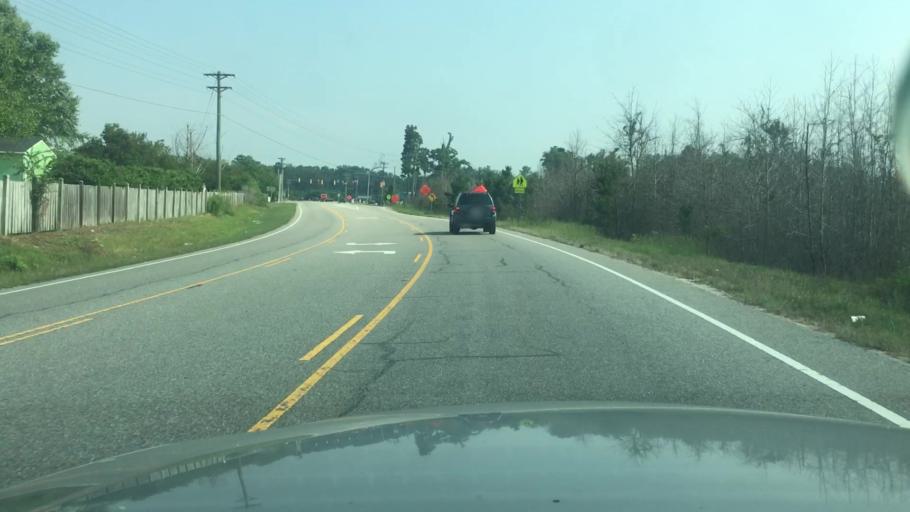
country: US
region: North Carolina
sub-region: Cumberland County
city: Hope Mills
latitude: 34.9228
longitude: -78.9096
